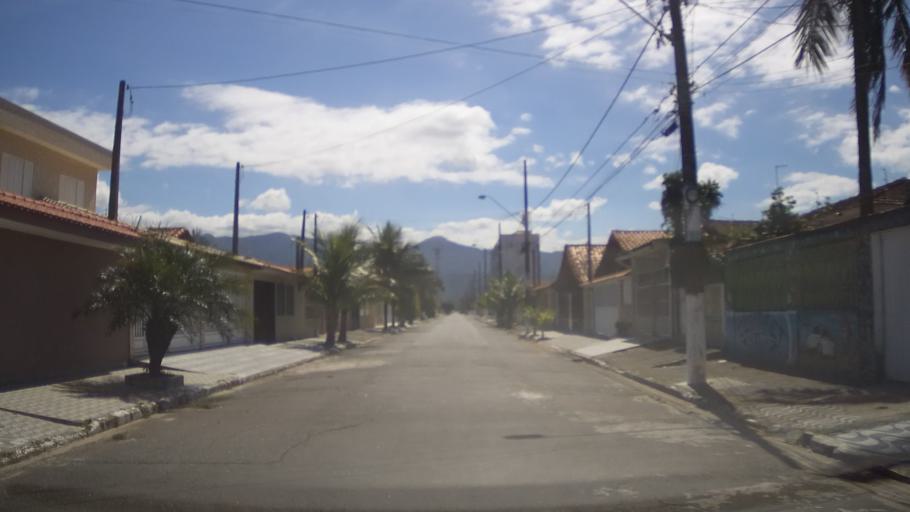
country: BR
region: Sao Paulo
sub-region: Praia Grande
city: Praia Grande
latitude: -24.0388
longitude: -46.4989
